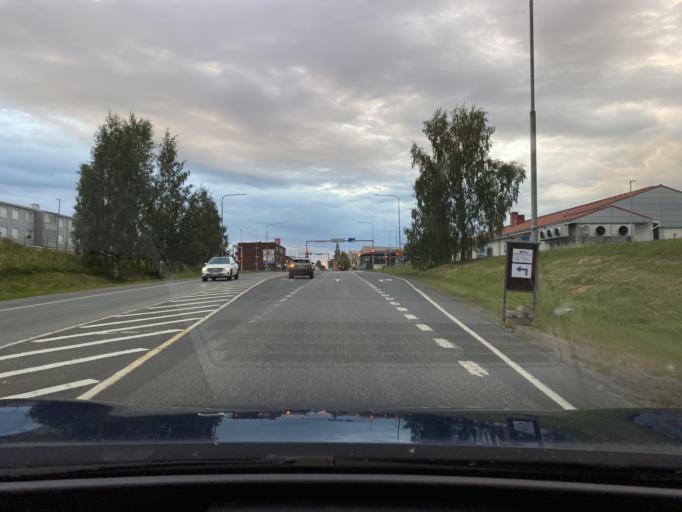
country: FI
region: Northern Ostrobothnia
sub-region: Raahe
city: Raahe
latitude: 64.6820
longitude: 24.4798
